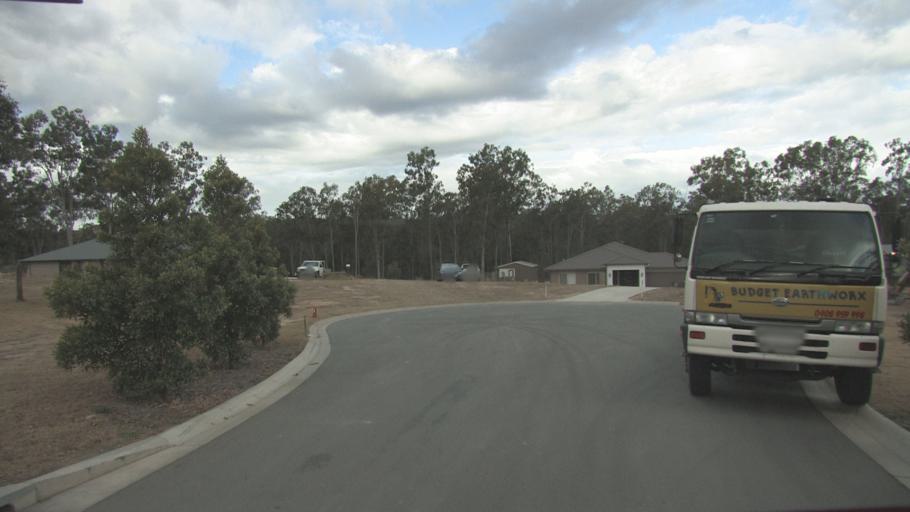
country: AU
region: Queensland
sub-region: Logan
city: Cedar Vale
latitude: -27.8603
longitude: 153.0854
